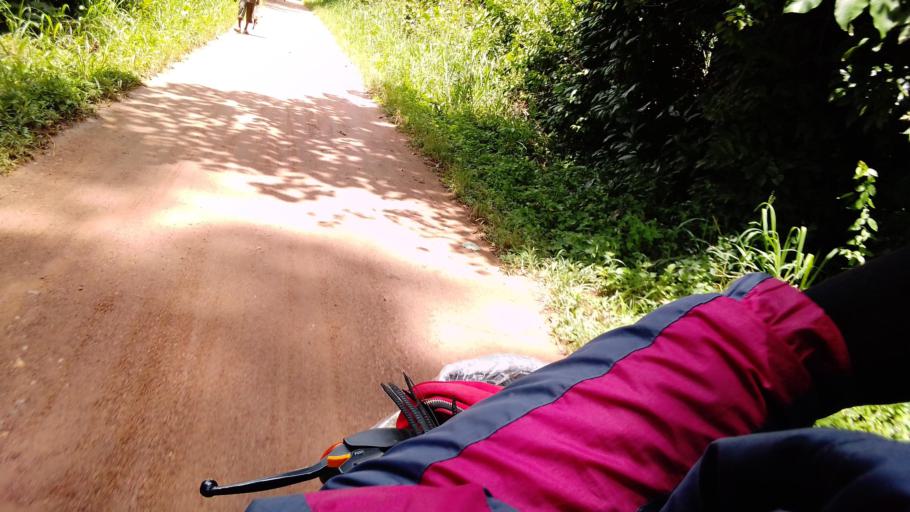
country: SL
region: Eastern Province
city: Koidu
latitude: 8.6967
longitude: -10.9536
